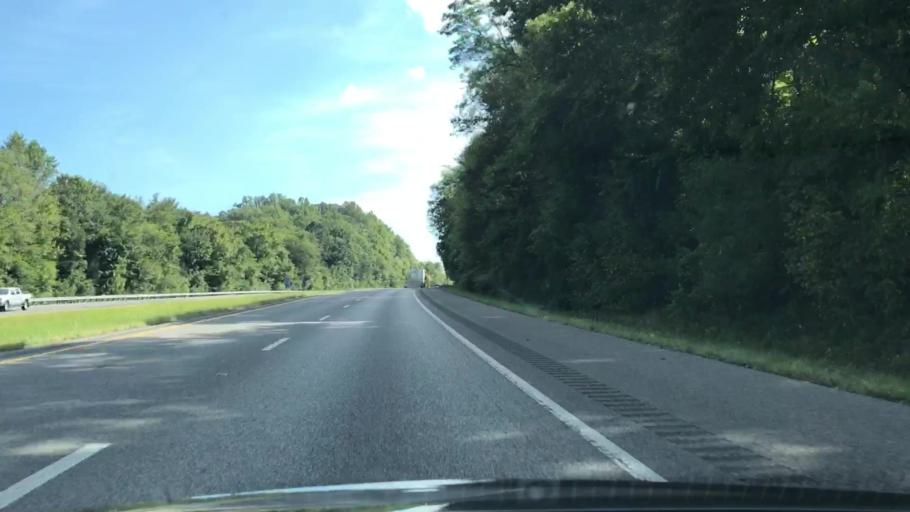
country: US
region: Alabama
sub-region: Limestone County
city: Ardmore
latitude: 35.1224
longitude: -86.8778
